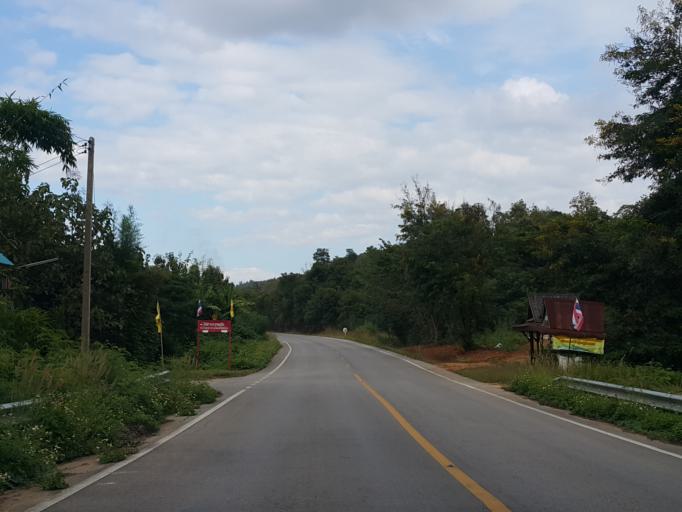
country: TH
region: Lampang
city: Chae Hom
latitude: 18.6338
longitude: 99.4923
